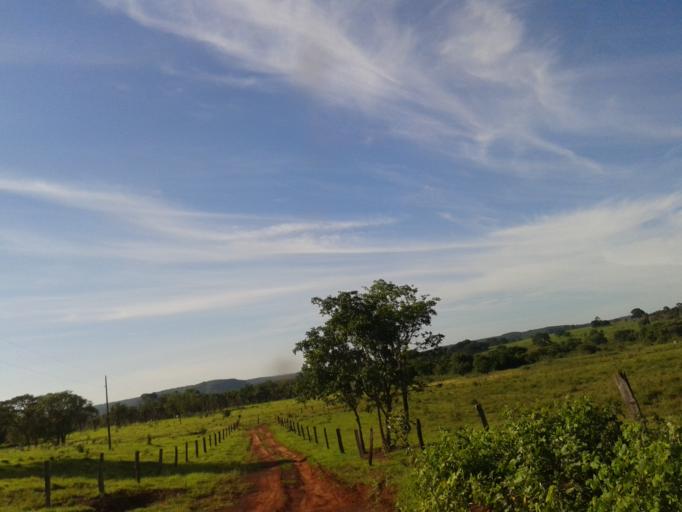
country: BR
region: Minas Gerais
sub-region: Santa Vitoria
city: Santa Vitoria
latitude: -19.0765
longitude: -49.9528
